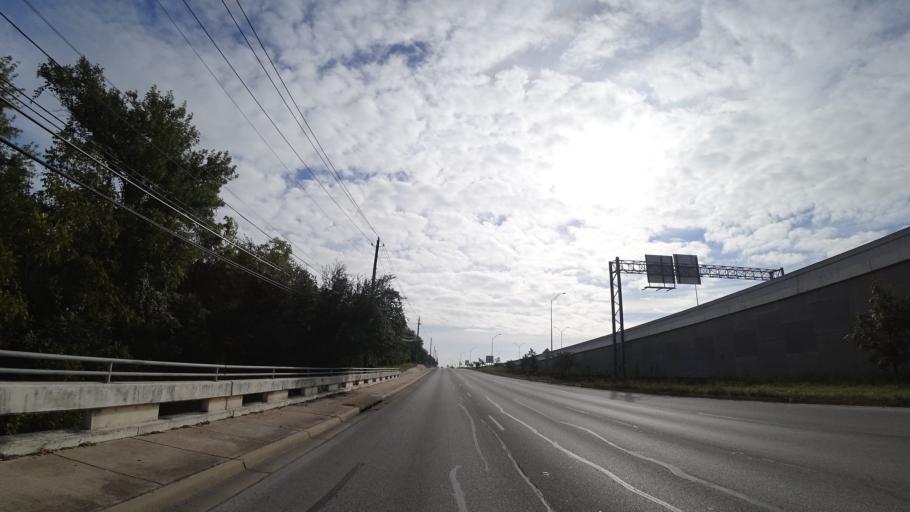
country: US
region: Texas
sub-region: Travis County
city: Austin
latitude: 30.2152
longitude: -97.7317
